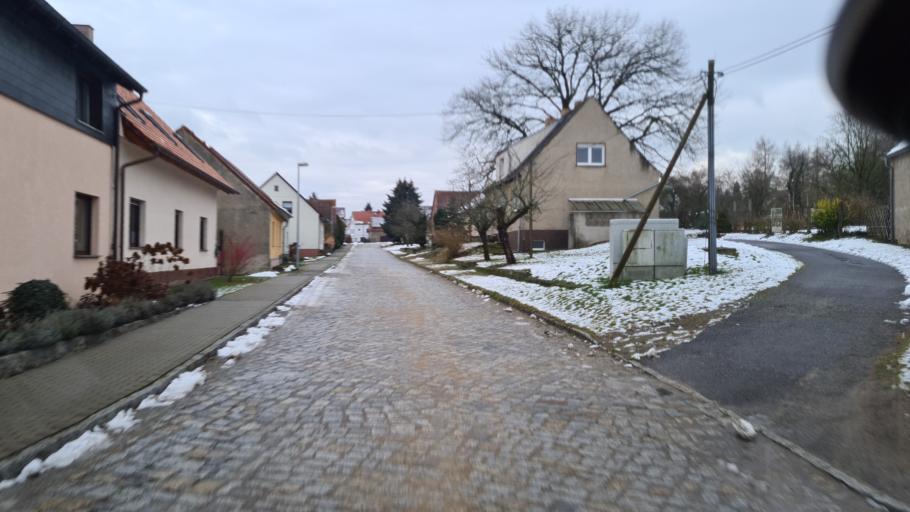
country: DE
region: Brandenburg
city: Schenkendobern
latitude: 51.9102
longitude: 14.5753
